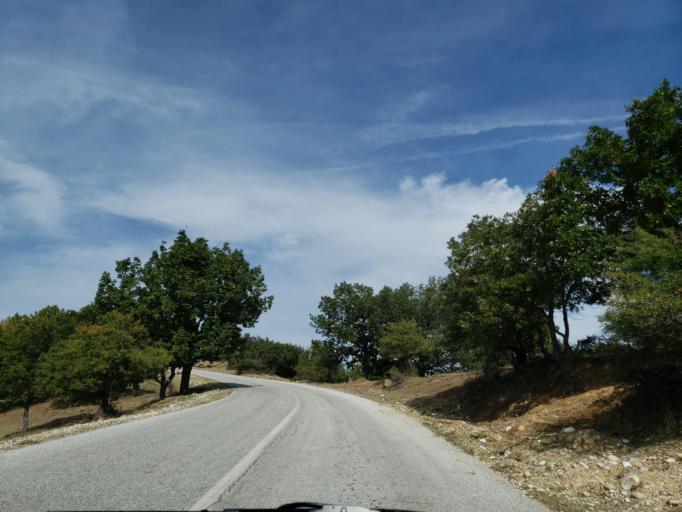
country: GR
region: Thessaly
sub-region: Trikala
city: Kastraki
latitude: 39.7610
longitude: 21.6630
